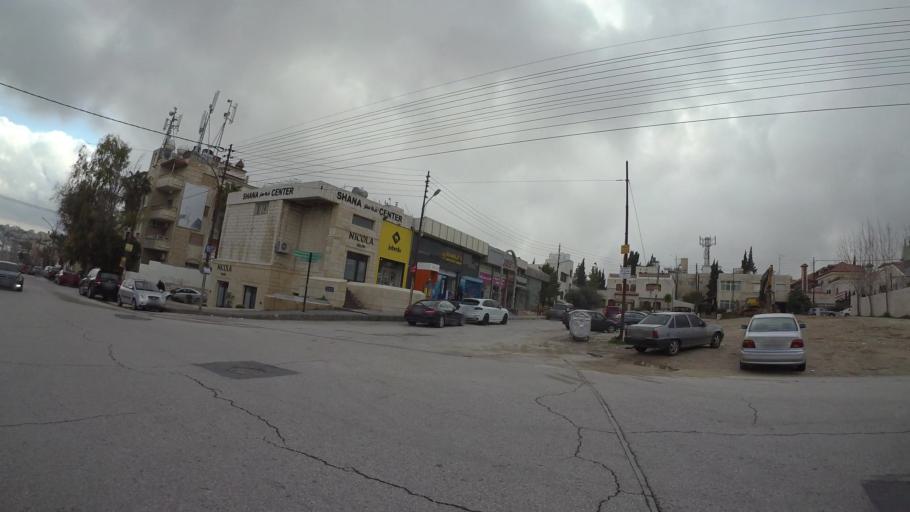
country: JO
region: Amman
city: Al Bunayyat ash Shamaliyah
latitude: 31.9502
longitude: 35.8838
